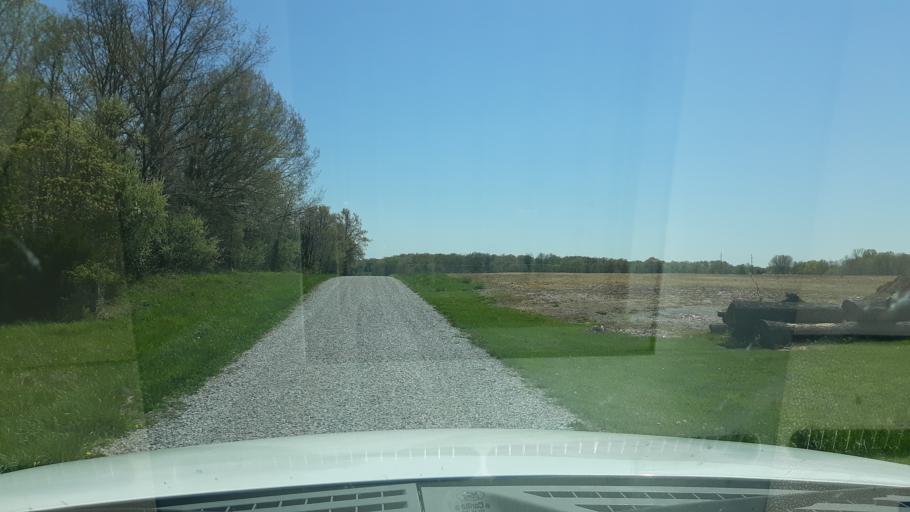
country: US
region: Illinois
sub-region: Saline County
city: Harrisburg
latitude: 37.8817
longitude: -88.6420
